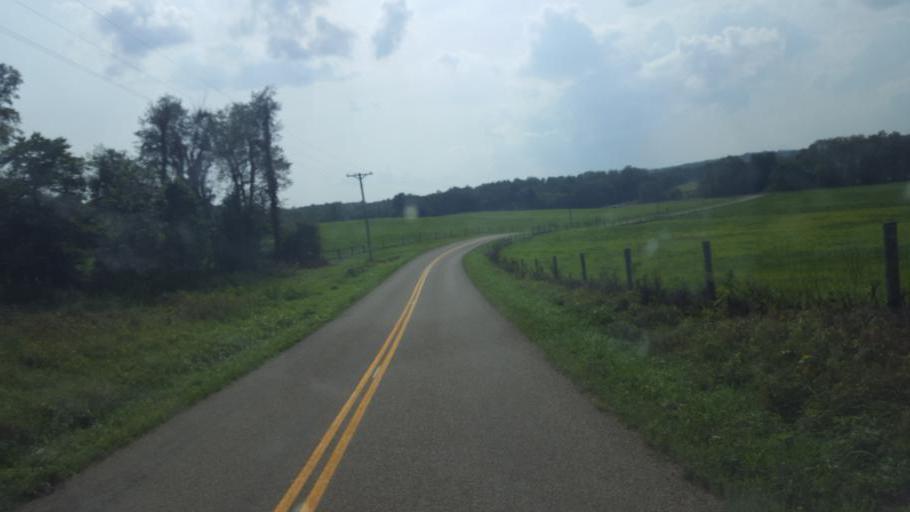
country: US
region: Ohio
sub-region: Knox County
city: Gambier
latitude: 40.3359
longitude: -82.3756
